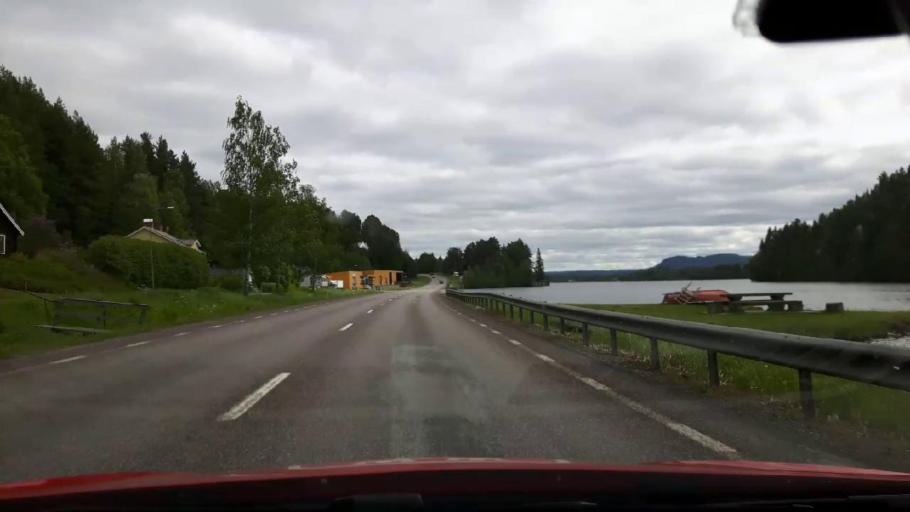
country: SE
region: Jaemtland
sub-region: Ragunda Kommun
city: Hammarstrand
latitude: 63.1388
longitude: 16.3410
